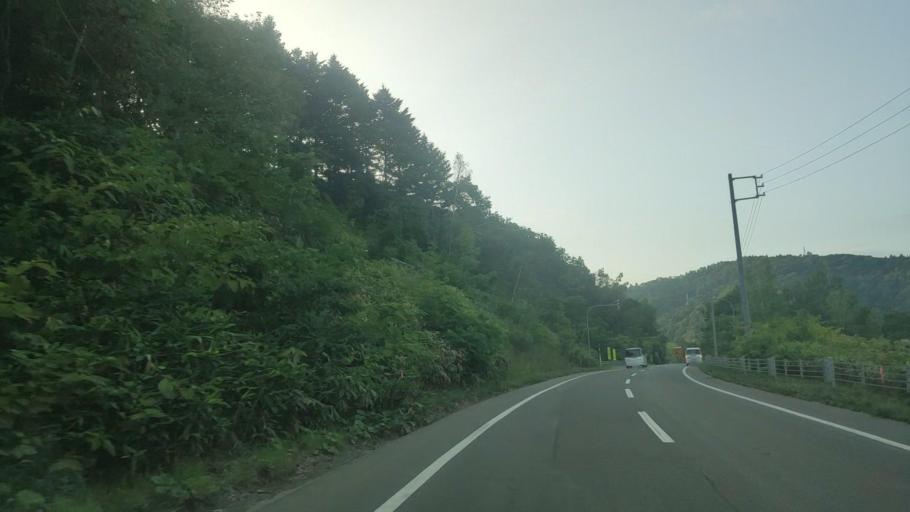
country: JP
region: Hokkaido
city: Bibai
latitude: 43.2296
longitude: 142.0402
